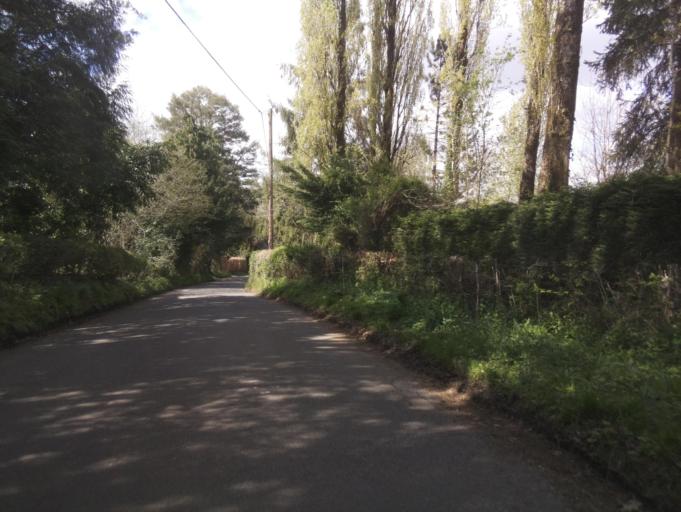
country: GB
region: England
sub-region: West Berkshire
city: Kintbury
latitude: 51.3736
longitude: -1.4827
